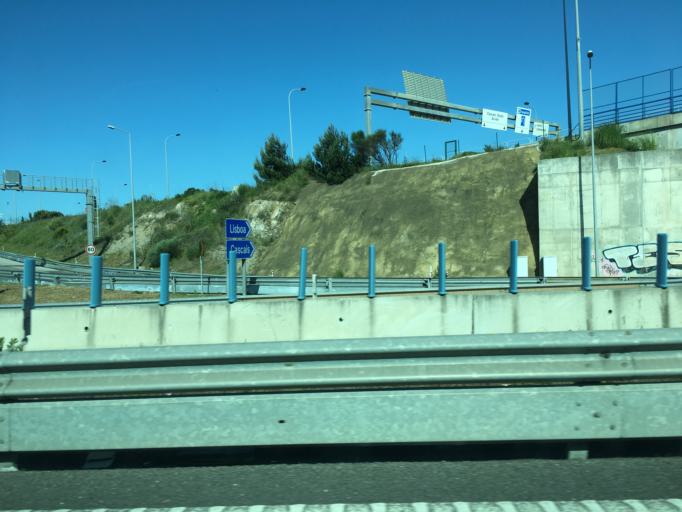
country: PT
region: Lisbon
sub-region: Cascais
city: Alcabideche
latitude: 38.7278
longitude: -9.4157
